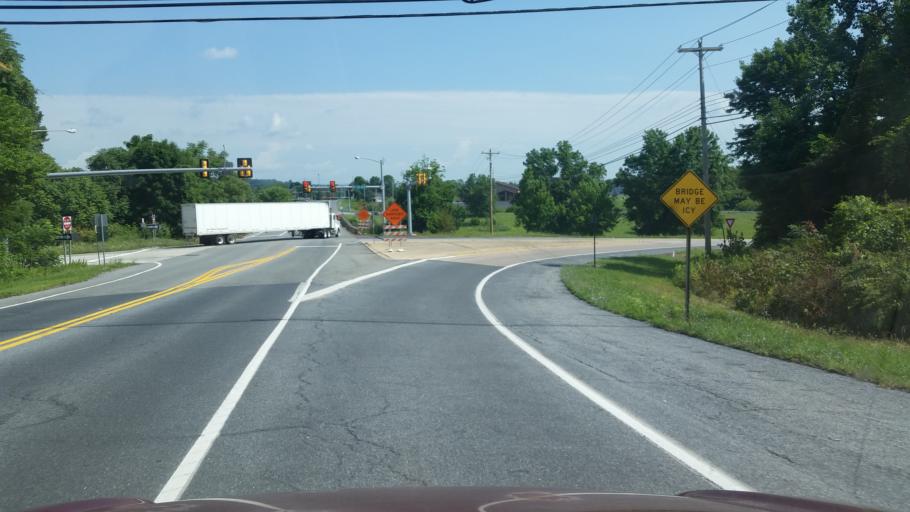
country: US
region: Pennsylvania
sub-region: Dauphin County
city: Middletown
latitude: 40.2256
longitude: -76.7373
